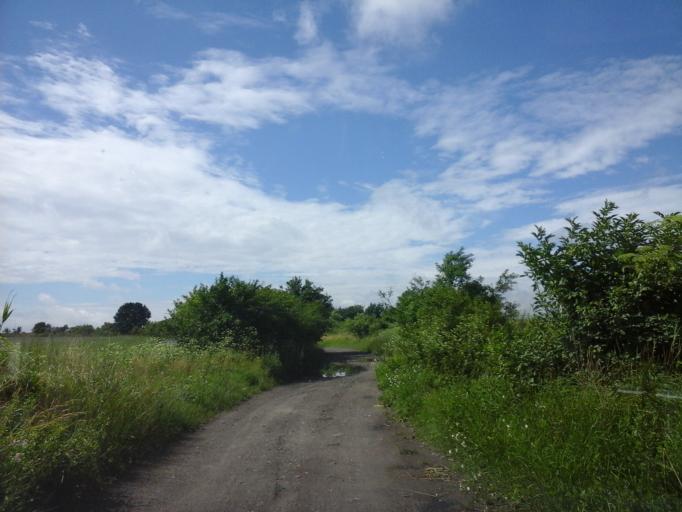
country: PL
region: West Pomeranian Voivodeship
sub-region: Powiat choszczenski
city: Krzecin
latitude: 53.0832
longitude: 15.4303
